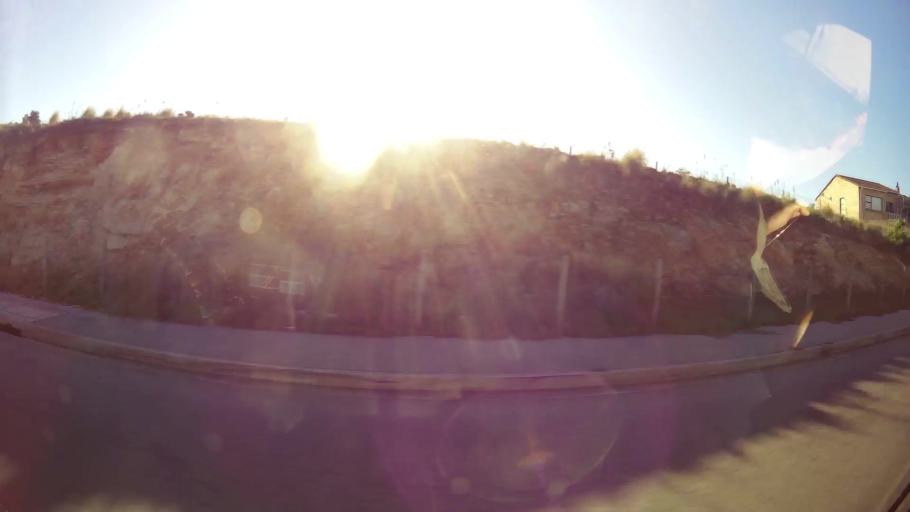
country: ZA
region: Eastern Cape
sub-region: Nelson Mandela Bay Metropolitan Municipality
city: Port Elizabeth
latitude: -33.9721
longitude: 25.6244
